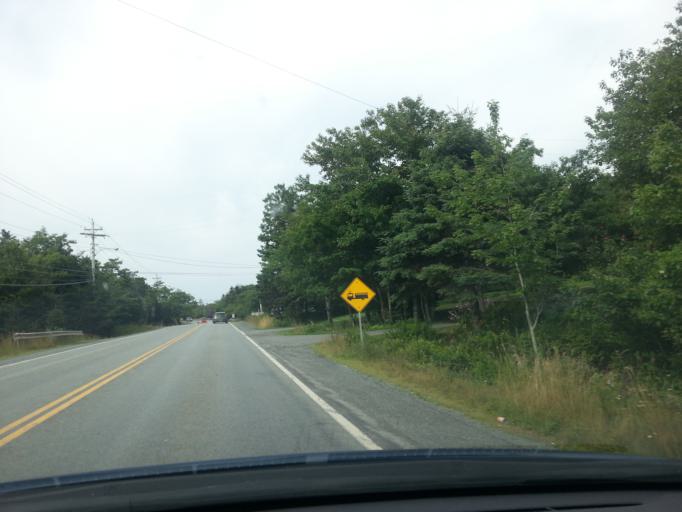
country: CA
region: Nova Scotia
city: Halifax
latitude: 44.5680
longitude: -63.7257
